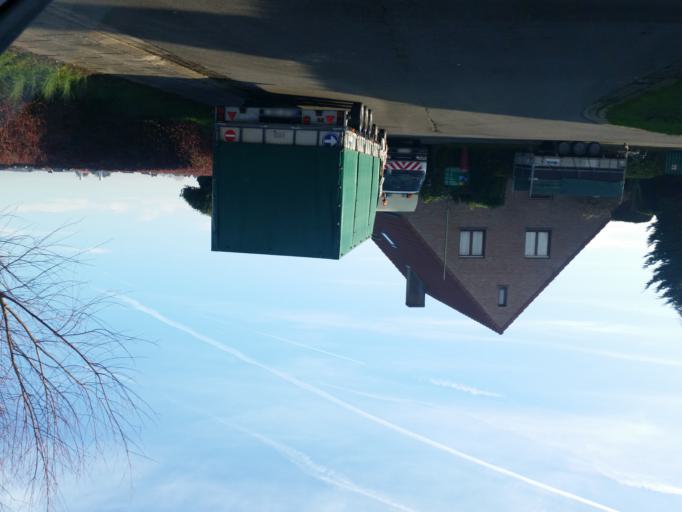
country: BE
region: Flanders
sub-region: Provincie West-Vlaanderen
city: De Haan
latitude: 51.2603
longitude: 3.0229
